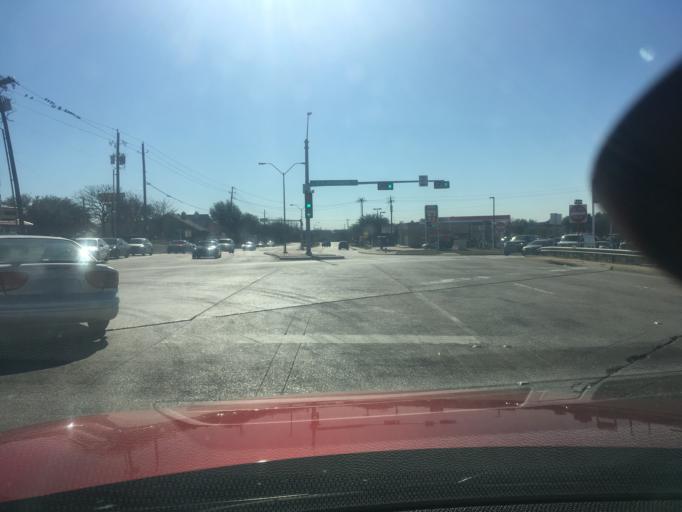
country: US
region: Texas
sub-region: Dallas County
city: Duncanville
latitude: 32.6408
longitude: -96.8915
